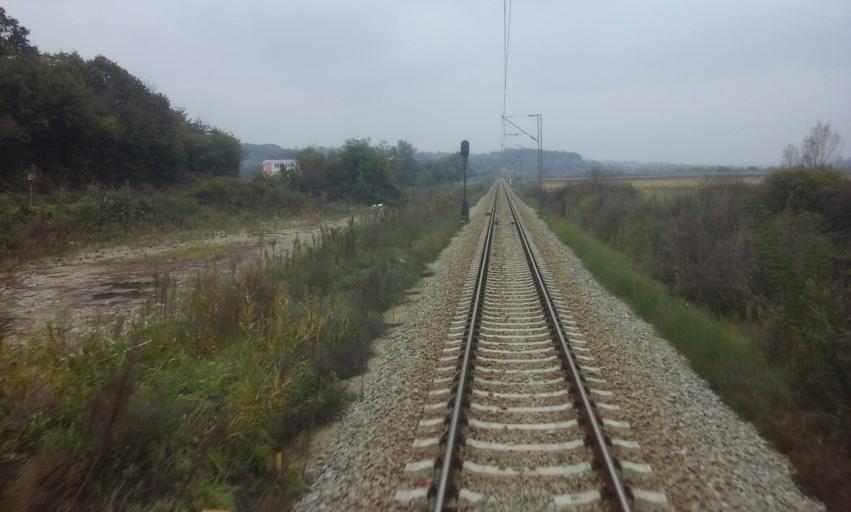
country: RS
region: Central Serbia
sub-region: Belgrade
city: Mladenovac
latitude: 44.4957
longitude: 20.6491
